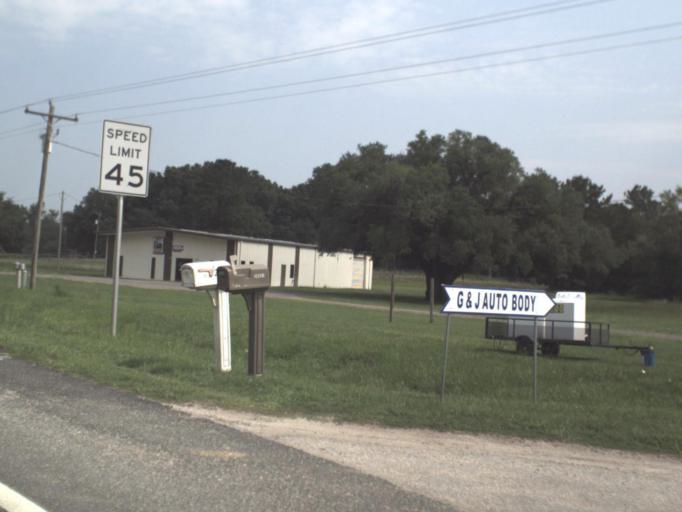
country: US
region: Florida
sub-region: Levy County
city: Williston
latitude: 29.3868
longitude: -82.4279
